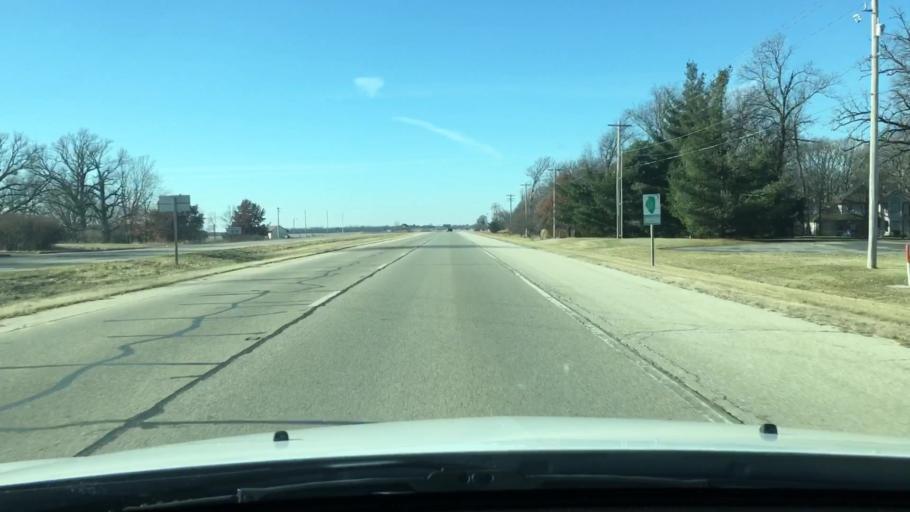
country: US
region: Illinois
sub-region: Woodford County
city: Metamora
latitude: 40.7792
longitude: -89.4096
